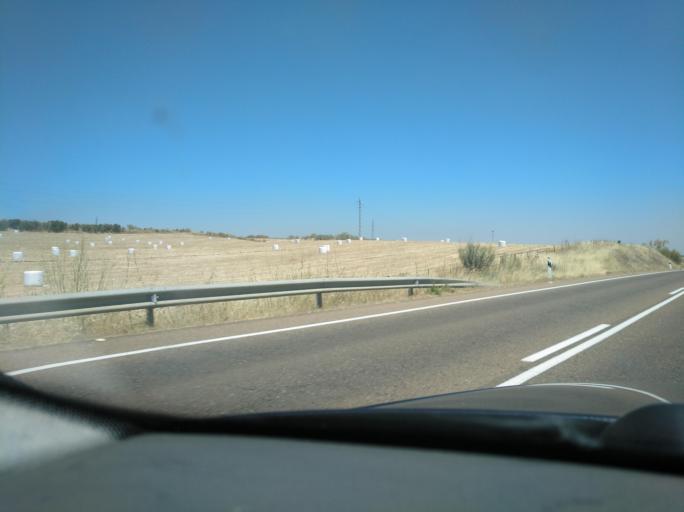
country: ES
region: Extremadura
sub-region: Provincia de Badajoz
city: Olivenza
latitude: 38.7279
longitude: -7.0748
